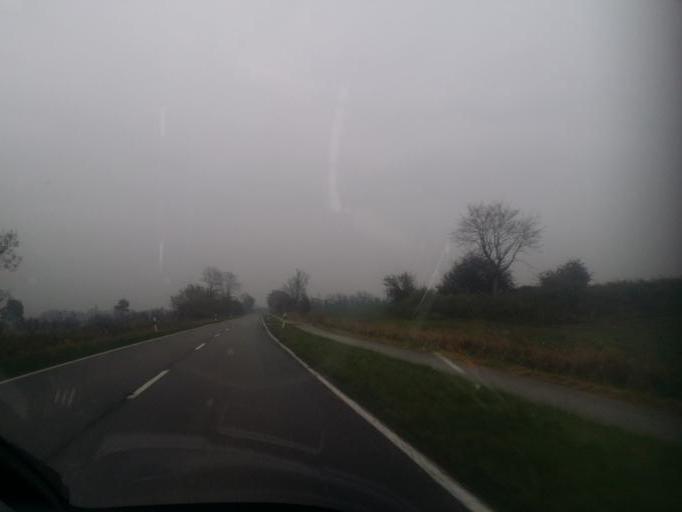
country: DE
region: Schleswig-Holstein
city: Grosssolt
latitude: 54.6934
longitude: 9.5000
